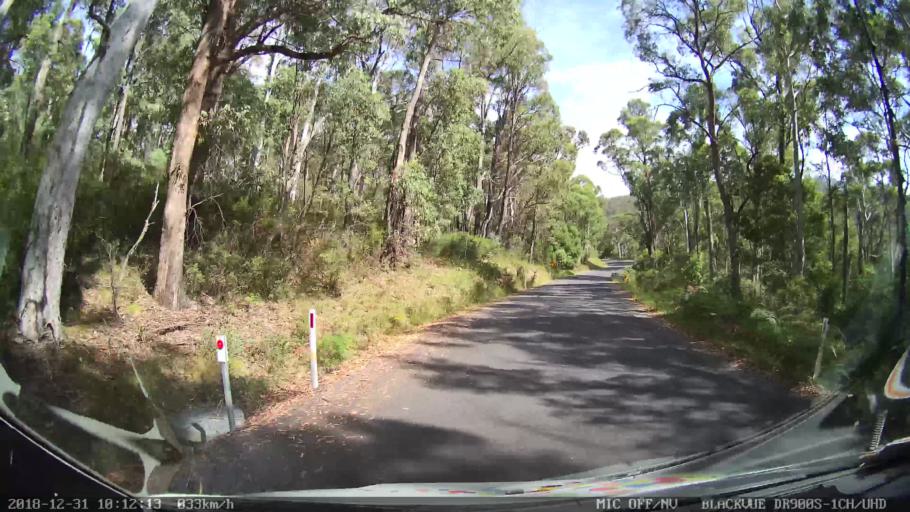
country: AU
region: New South Wales
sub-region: Snowy River
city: Jindabyne
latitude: -36.5376
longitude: 148.1625
